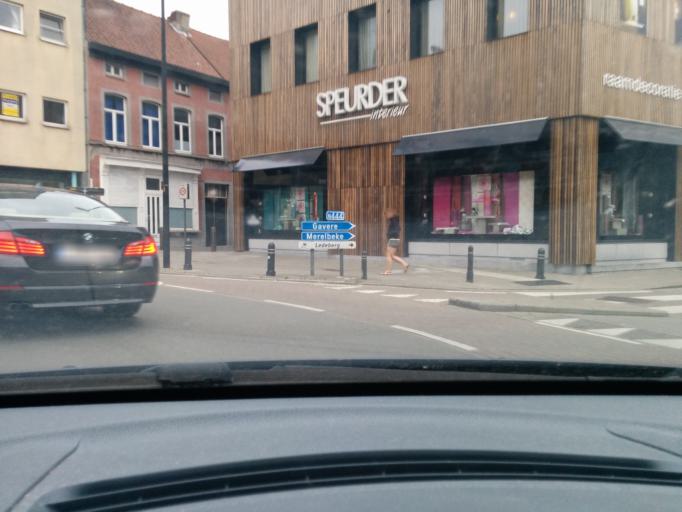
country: BE
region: Flanders
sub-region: Provincie Oost-Vlaanderen
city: Ledeberg
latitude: 51.0369
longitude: 3.7389
